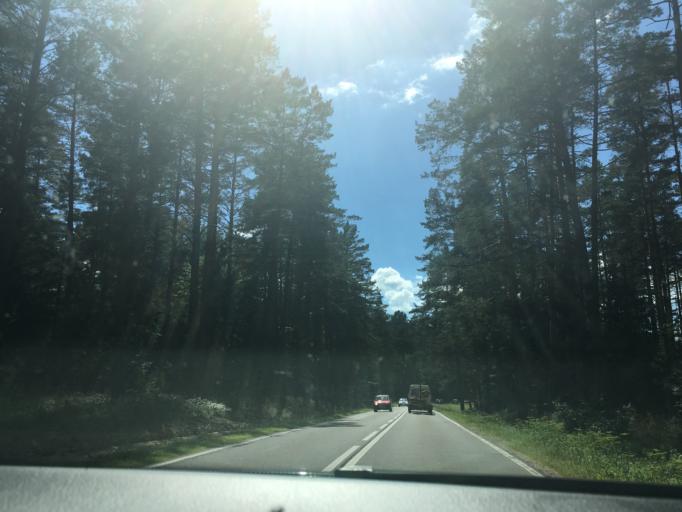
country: PL
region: Podlasie
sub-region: Powiat augustowski
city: Augustow
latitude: 53.8570
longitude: 23.0763
